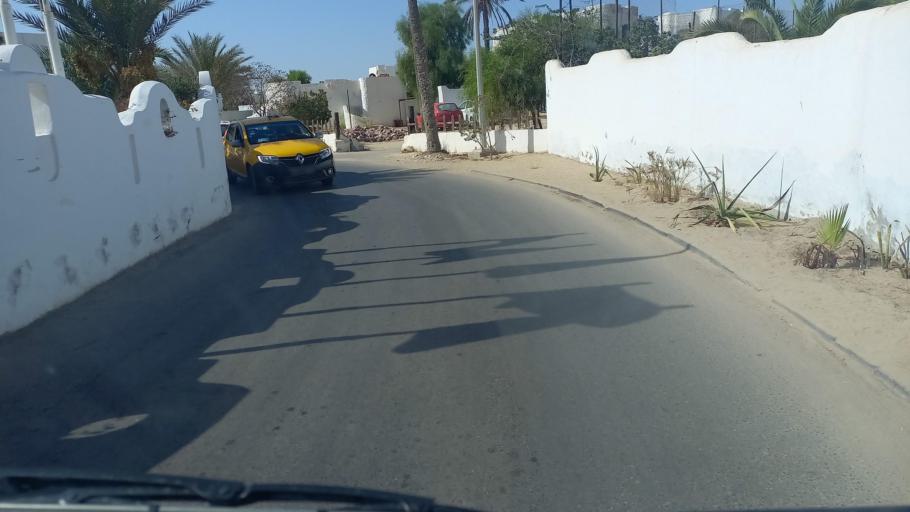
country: TN
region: Madanin
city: Midoun
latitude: 33.8497
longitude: 10.9882
